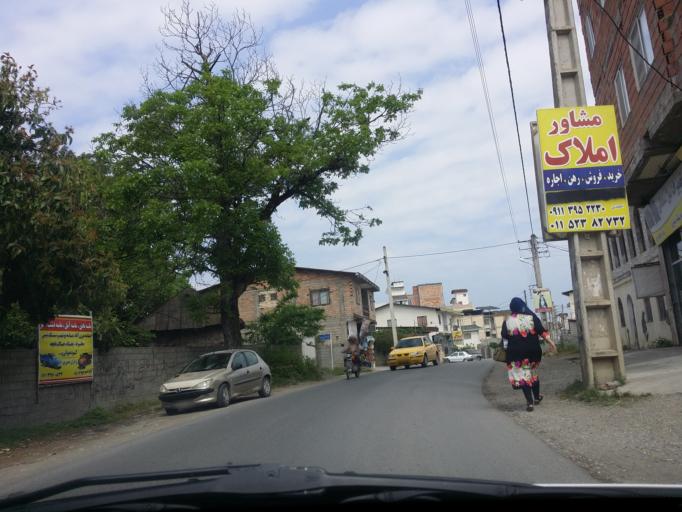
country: IR
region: Mazandaran
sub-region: Nowshahr
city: Nowshahr
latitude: 36.6272
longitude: 51.4856
